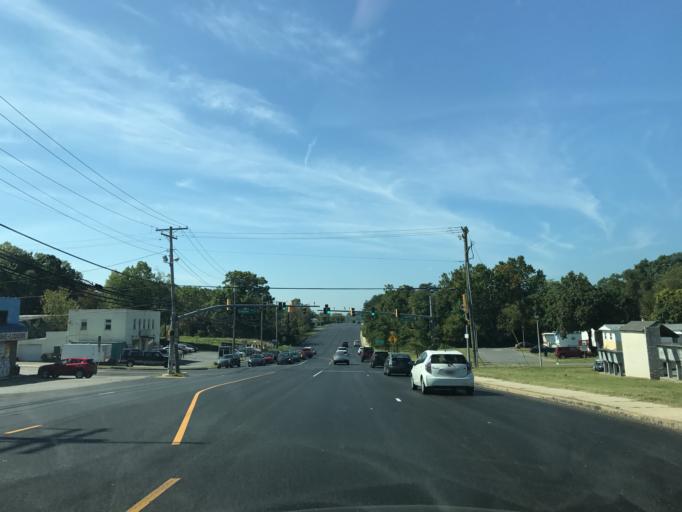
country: US
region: Maryland
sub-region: Howard County
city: West Elkridge
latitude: 39.1988
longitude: -76.7395
